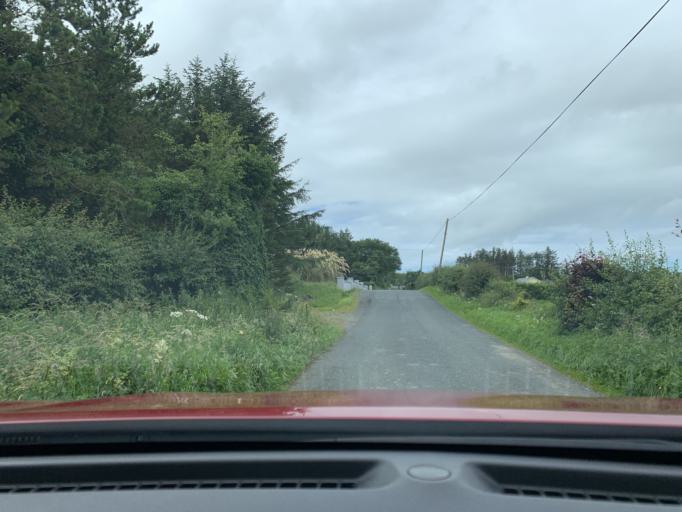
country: IE
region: Connaught
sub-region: Sligo
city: Sligo
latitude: 54.3992
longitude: -8.4271
